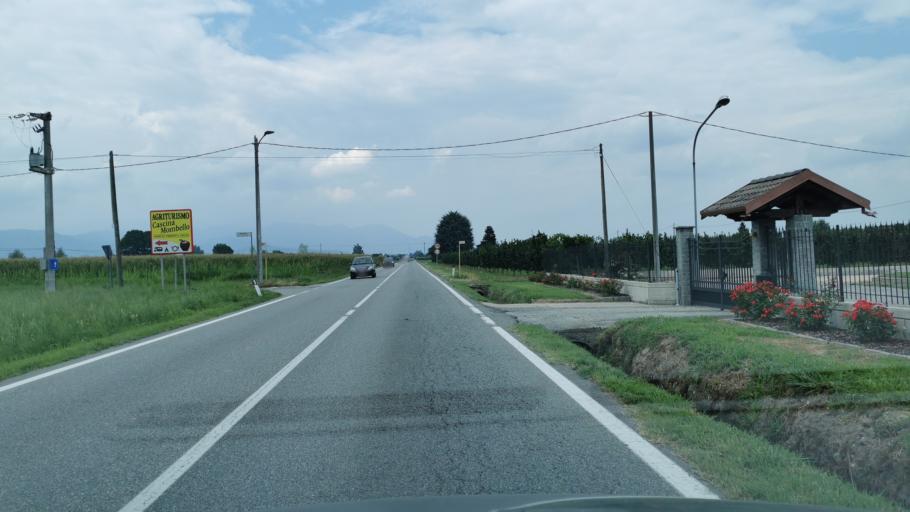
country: IT
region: Piedmont
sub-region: Provincia di Torino
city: Cavour
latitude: 44.8083
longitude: 7.3725
